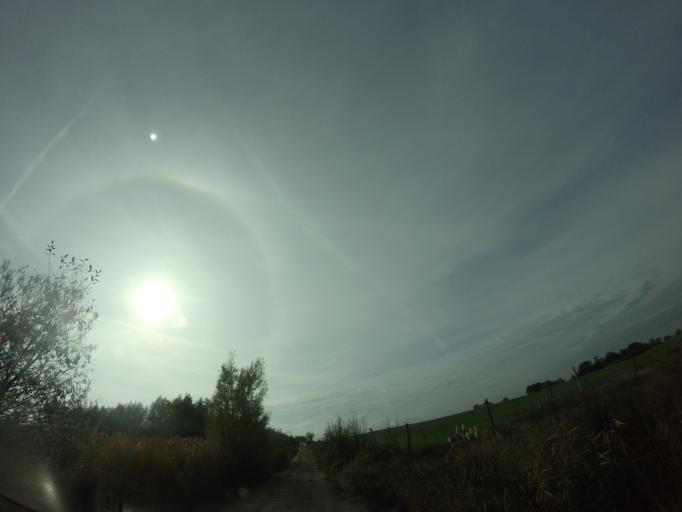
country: PL
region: West Pomeranian Voivodeship
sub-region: Powiat choszczenski
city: Drawno
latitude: 53.2407
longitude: 15.7334
